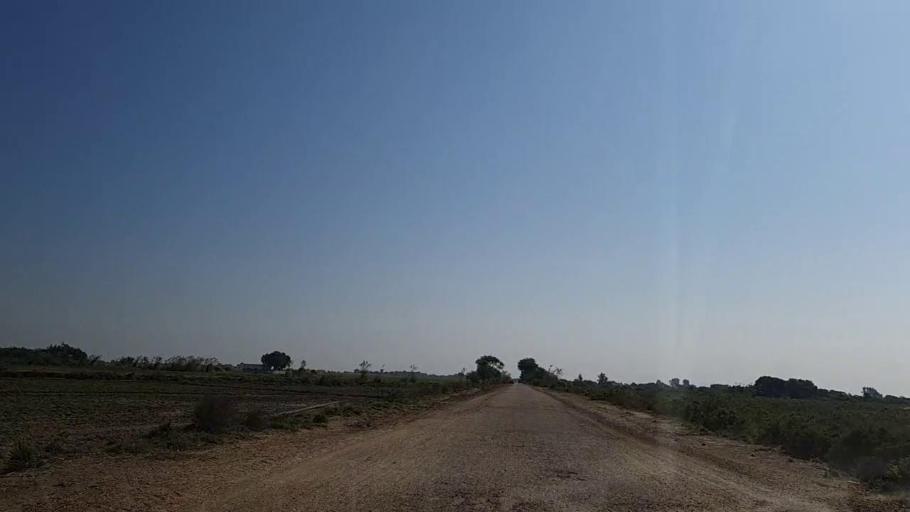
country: PK
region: Sindh
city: Chuhar Jamali
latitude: 24.5260
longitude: 68.0853
